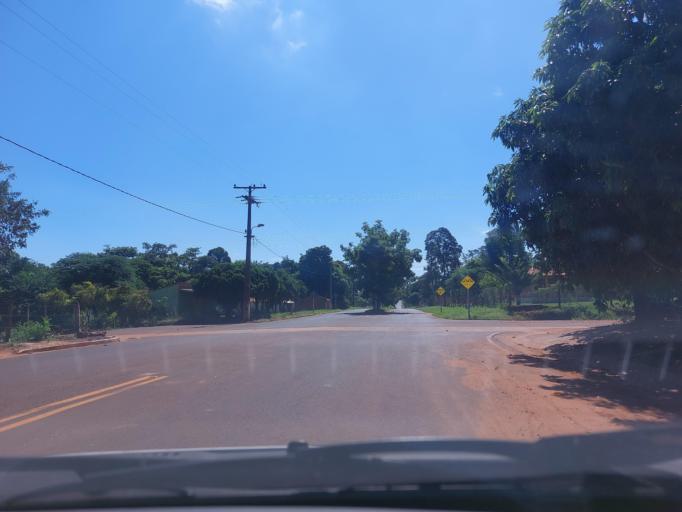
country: PY
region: San Pedro
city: Guayaybi
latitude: -24.5683
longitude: -56.5195
